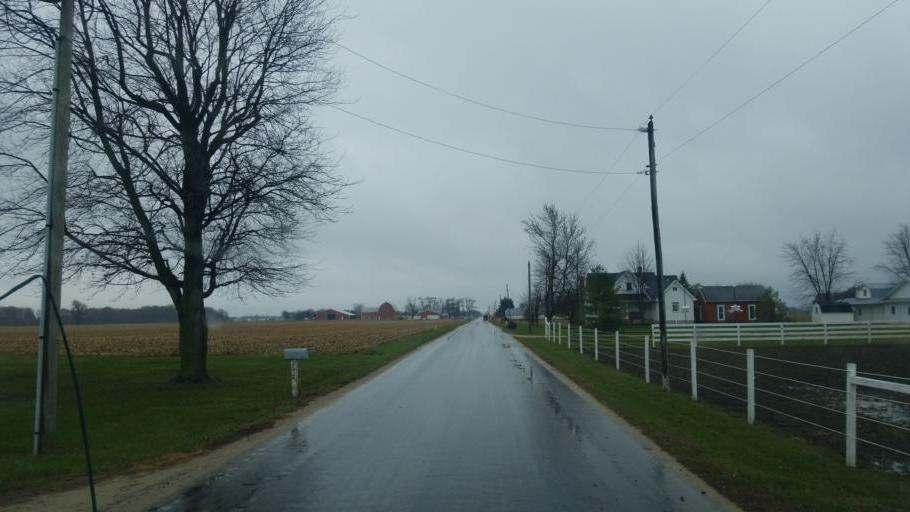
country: US
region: Indiana
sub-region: Adams County
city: Berne
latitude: 40.7079
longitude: -84.9173
